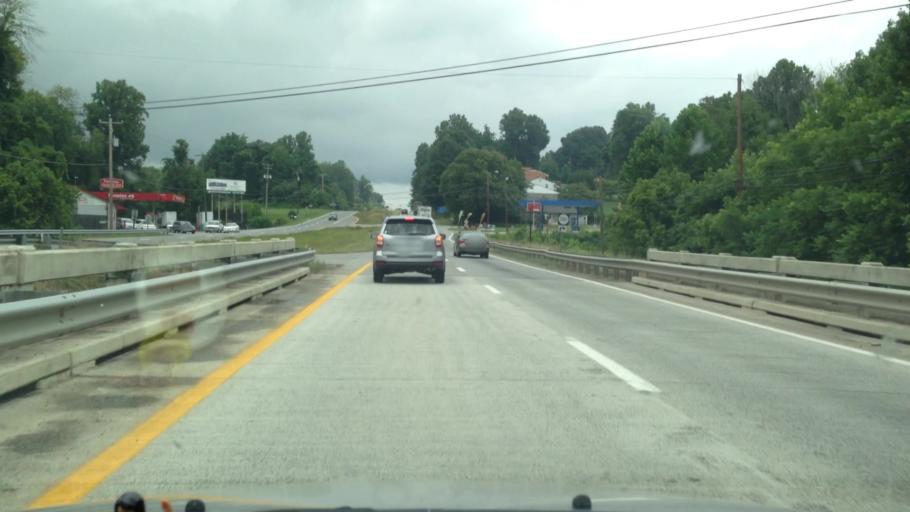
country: US
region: Virginia
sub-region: Henry County
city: Chatmoss
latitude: 36.6129
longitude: -79.8609
